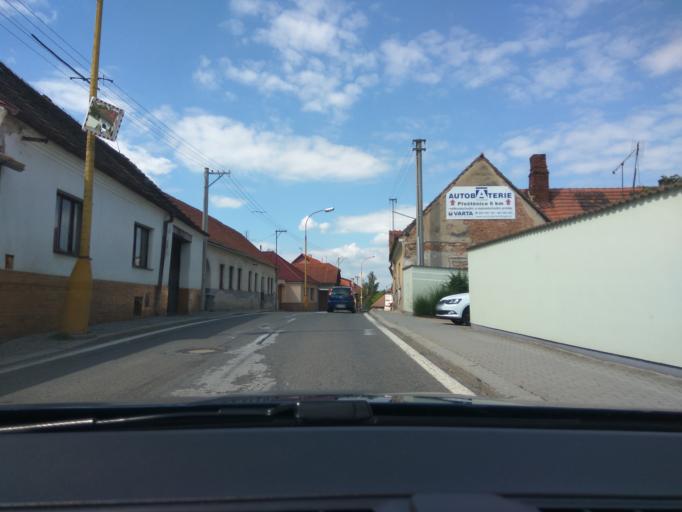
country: CZ
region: Jihocesky
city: Milevsko
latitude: 49.4458
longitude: 14.3602
